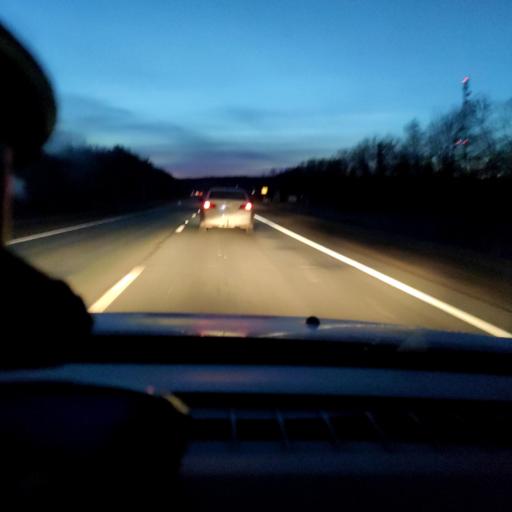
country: RU
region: Samara
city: Novokuybyshevsk
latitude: 52.9846
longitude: 49.8732
